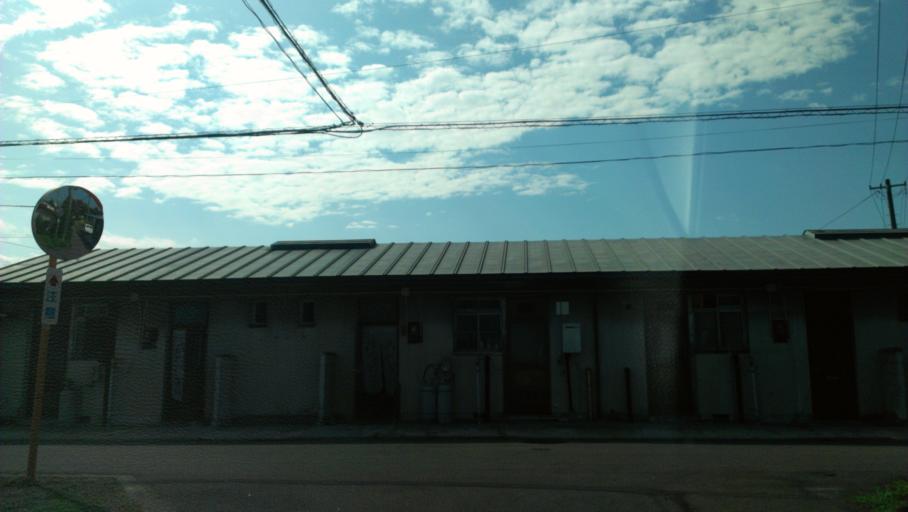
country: JP
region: Fukushima
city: Kitakata
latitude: 37.4957
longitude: 139.9130
